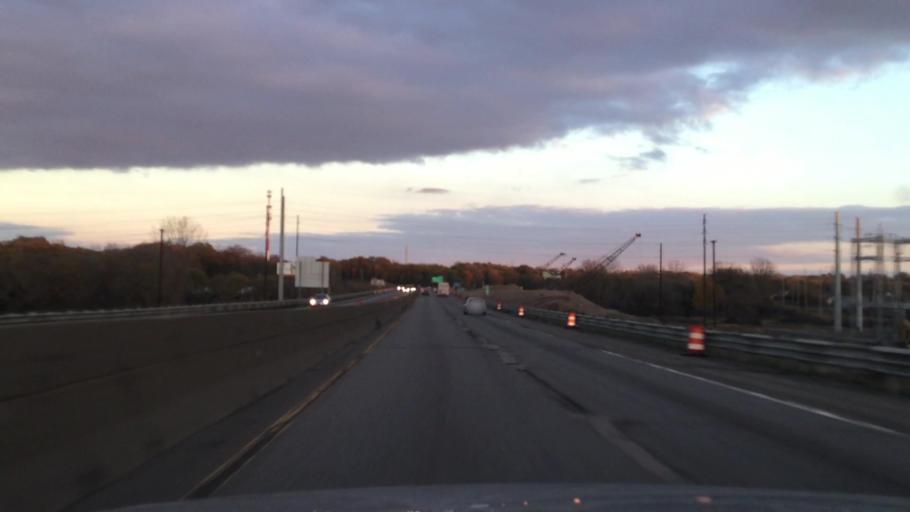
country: US
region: Michigan
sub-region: Jackson County
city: Jackson
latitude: 42.2721
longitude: -84.4137
